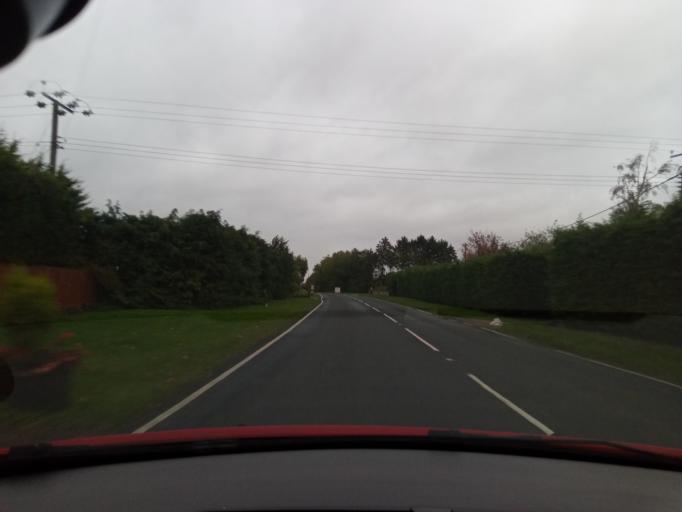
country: GB
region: England
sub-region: Essex
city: Great Yeldham
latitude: 52.0261
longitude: 0.5473
